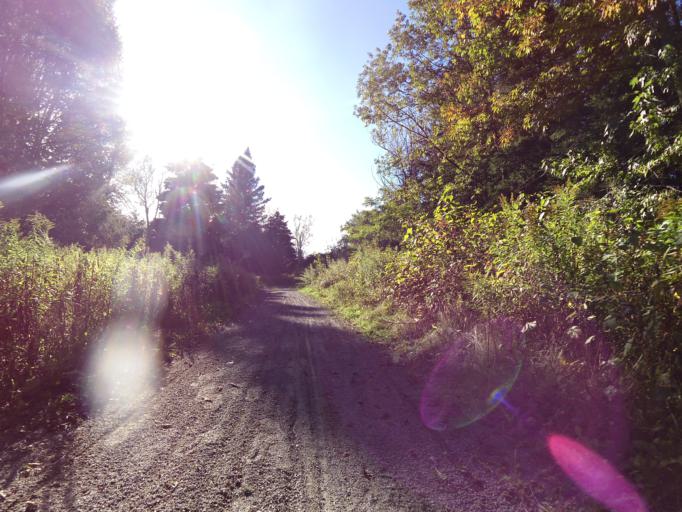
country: CA
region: Ontario
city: Oshawa
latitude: 43.8743
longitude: -78.7876
